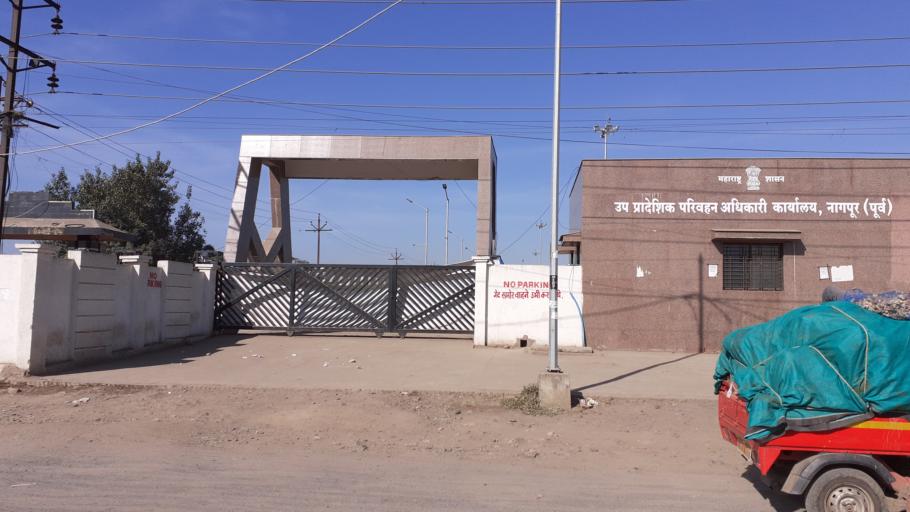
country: IN
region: Maharashtra
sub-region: Nagpur Division
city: Nagpur
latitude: 21.1633
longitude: 79.1379
